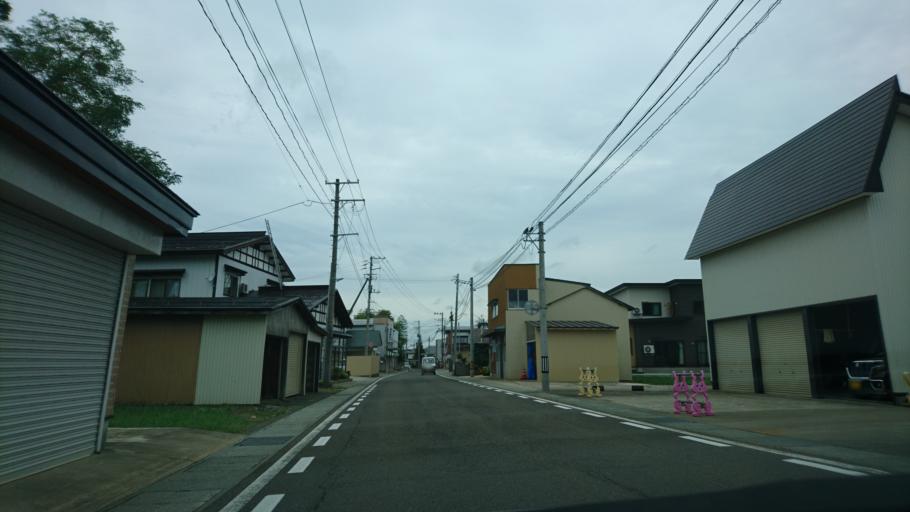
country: JP
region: Akita
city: Yuzawa
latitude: 39.1659
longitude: 140.5608
